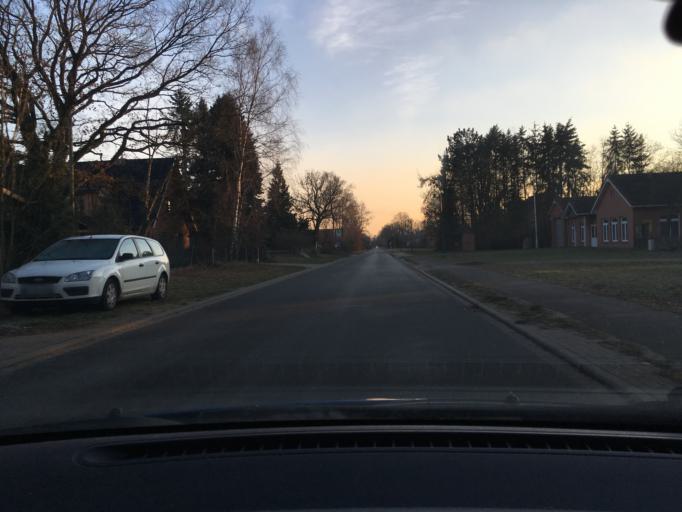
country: DE
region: Schleswig-Holstein
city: Langenlehsten
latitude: 53.5008
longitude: 10.7409
